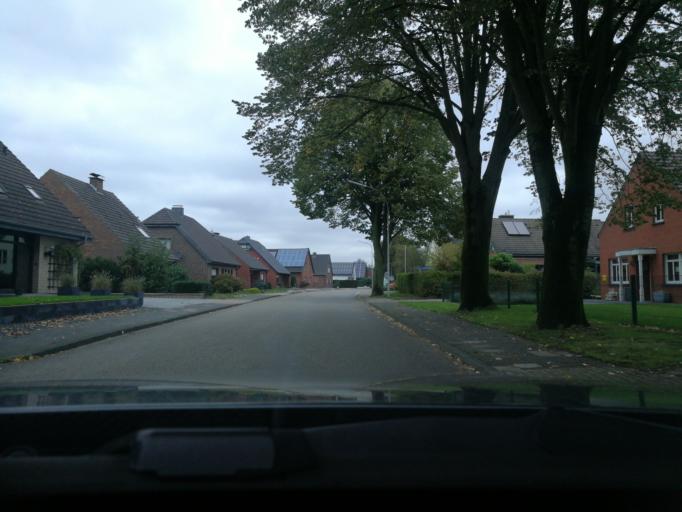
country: DE
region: North Rhine-Westphalia
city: Straelen
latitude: 51.5012
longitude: 6.2427
